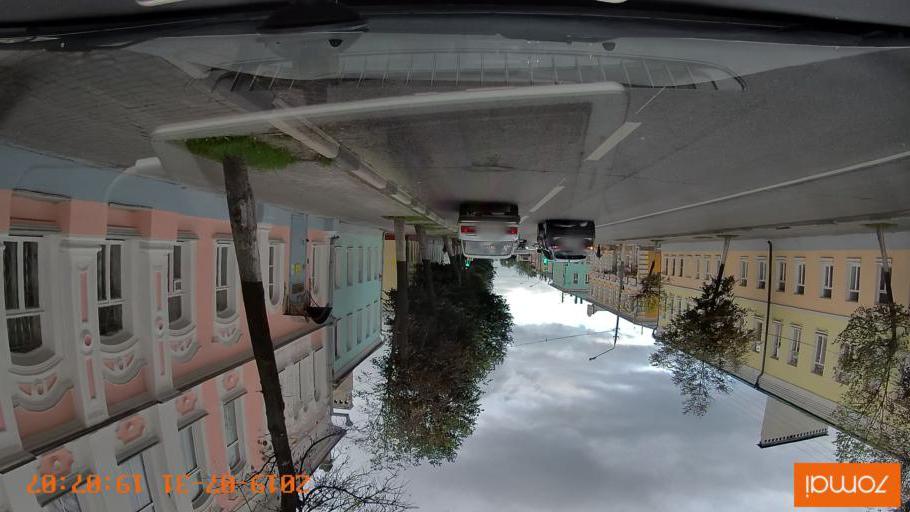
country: RU
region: Moskovskaya
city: Kolomna
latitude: 55.0992
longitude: 38.7588
